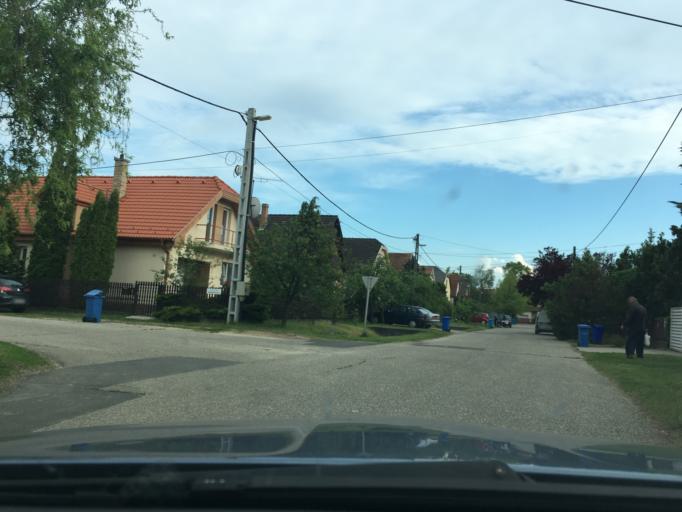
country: HU
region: Hajdu-Bihar
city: Debrecen
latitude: 47.5494
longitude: 21.6726
